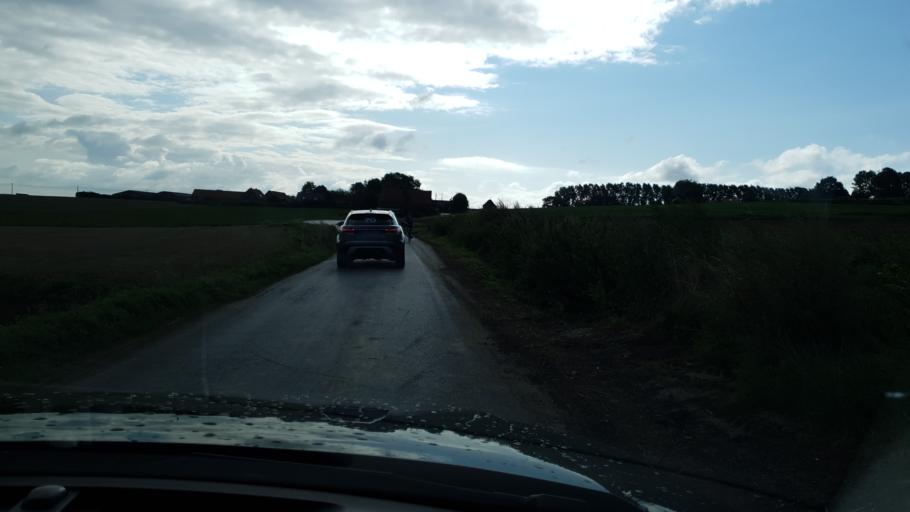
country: BE
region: Wallonia
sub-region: Province du Hainaut
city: Tournai
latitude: 50.6607
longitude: 3.4190
